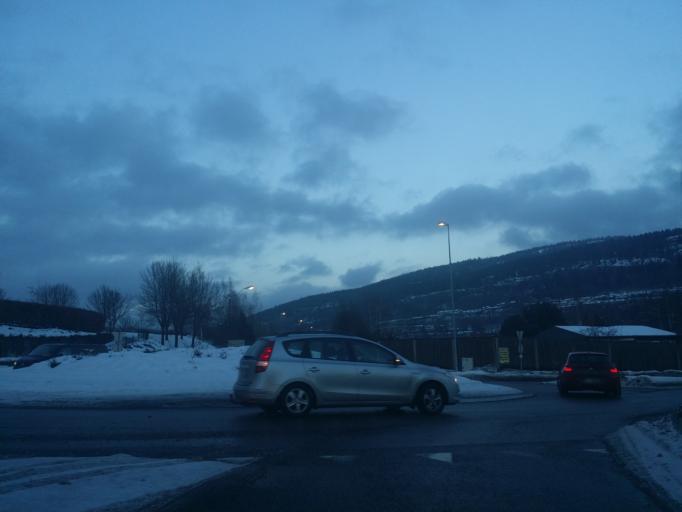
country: NO
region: Akershus
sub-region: Baerum
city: Skui
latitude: 59.9201
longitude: 10.4892
